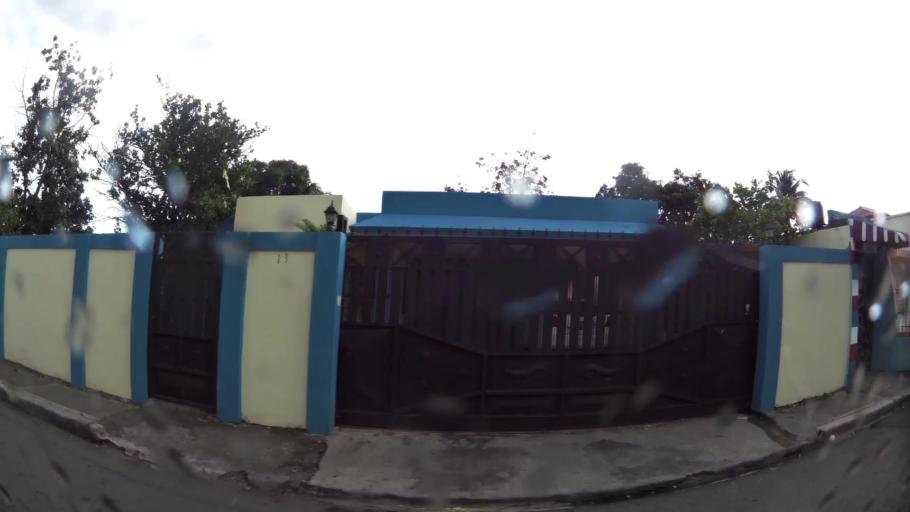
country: DO
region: Monsenor Nouel
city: Bonao
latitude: 18.9316
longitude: -70.4057
